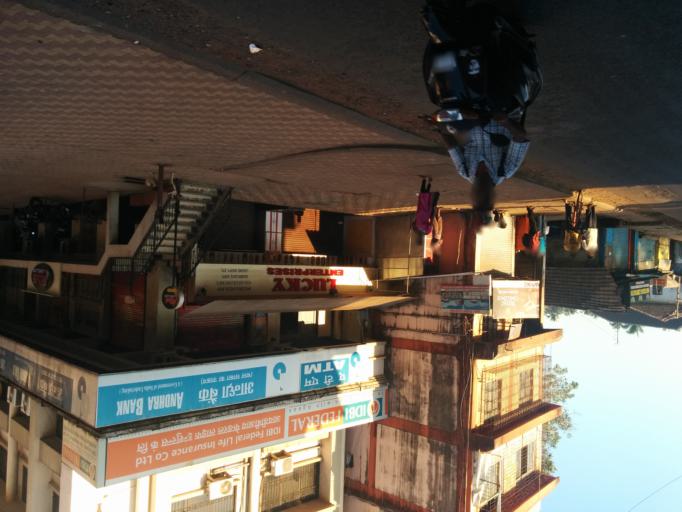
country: IN
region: Goa
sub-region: South Goa
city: Madgaon
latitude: 15.2700
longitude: 73.9589
